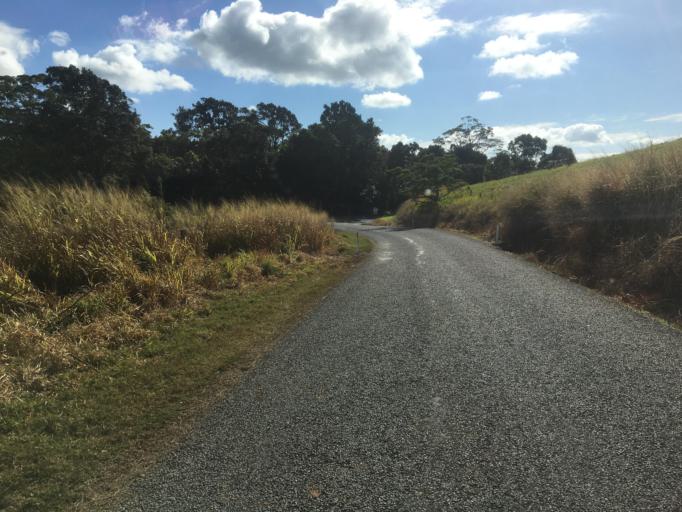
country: AU
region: Queensland
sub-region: Tablelands
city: Ravenshoe
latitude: -17.5322
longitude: 145.6090
